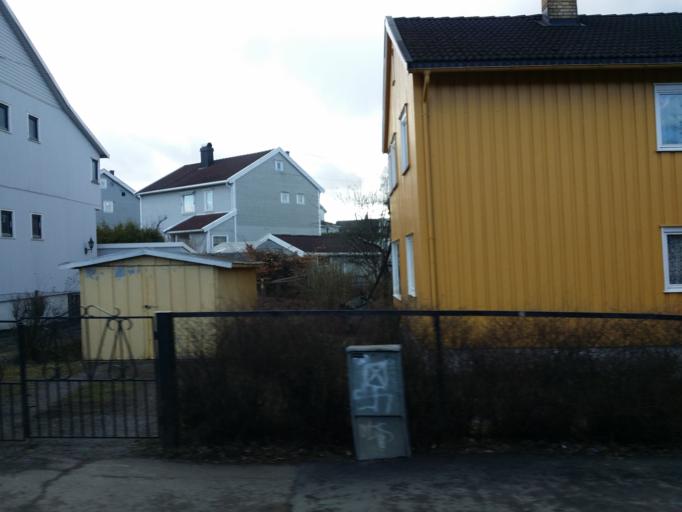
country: NO
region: Oslo
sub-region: Oslo
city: Oslo
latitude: 59.9600
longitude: 10.7848
